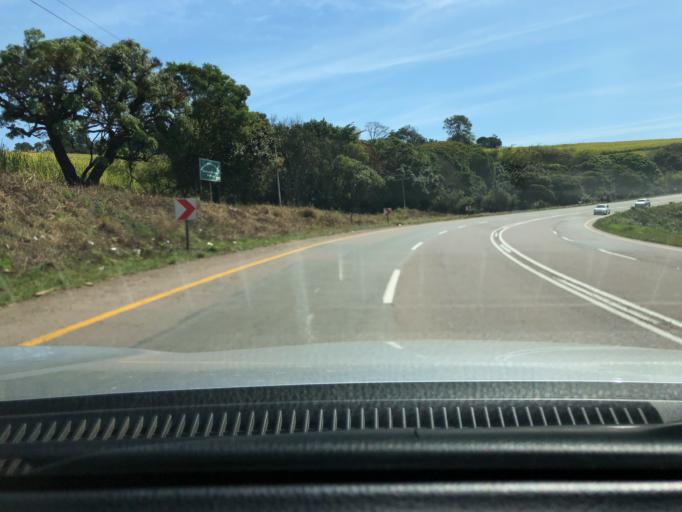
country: ZA
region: KwaZulu-Natal
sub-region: uMgungundlovu District Municipality
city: Richmond
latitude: -29.8193
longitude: 30.3422
